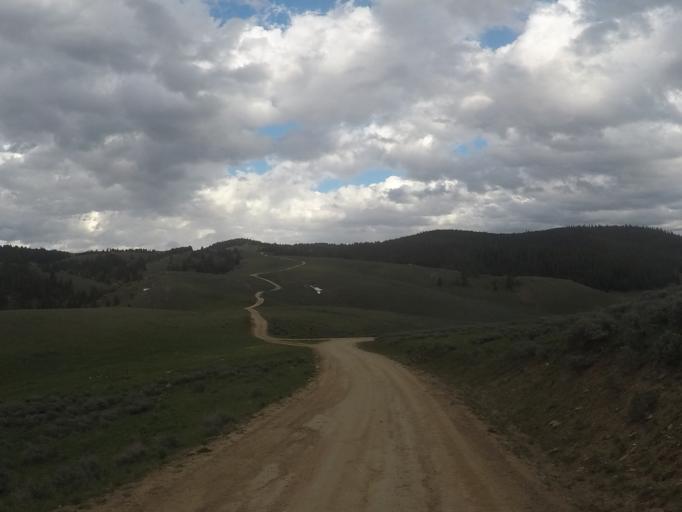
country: US
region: Wyoming
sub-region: Sheridan County
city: Sheridan
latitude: 44.5061
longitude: -107.4556
